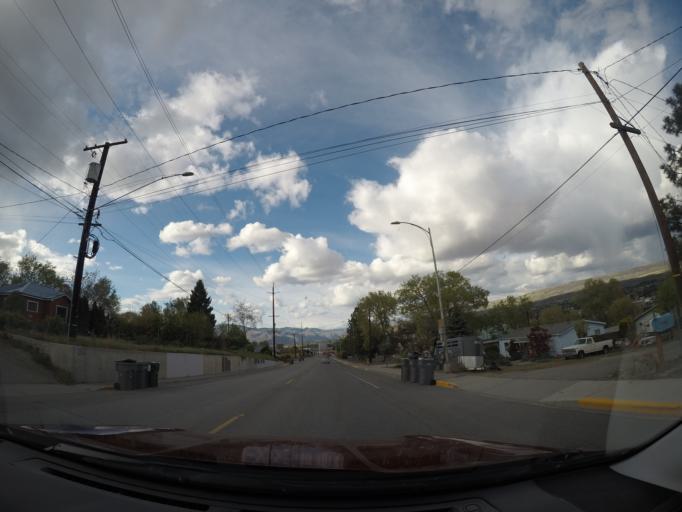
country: US
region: Washington
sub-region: Douglas County
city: East Wenatchee
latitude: 47.4062
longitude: -120.3030
